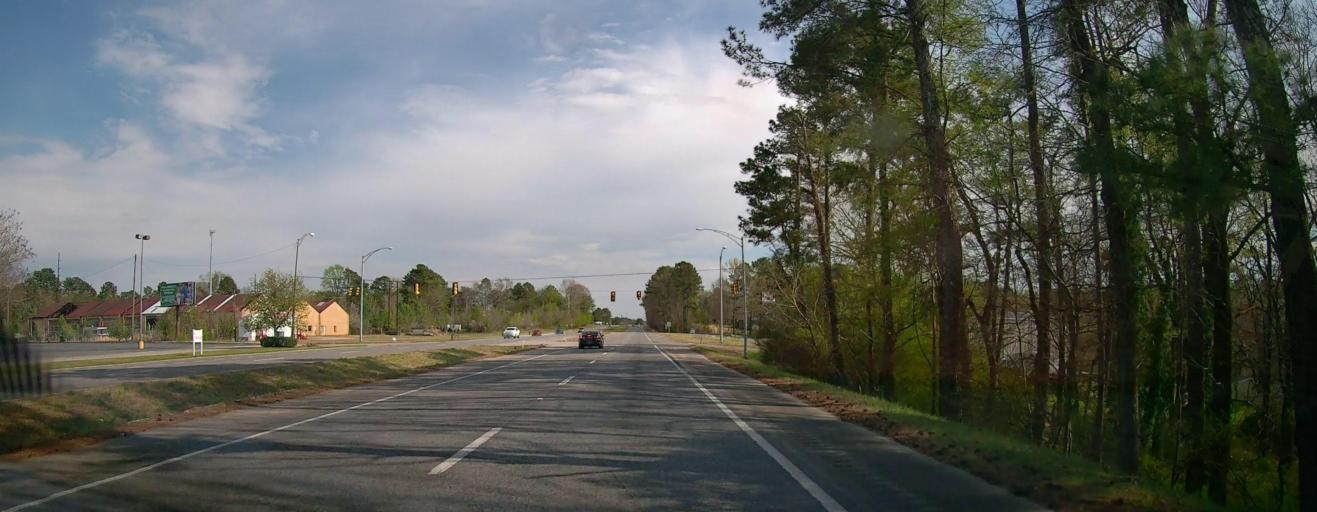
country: US
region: Alabama
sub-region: Jefferson County
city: Adamsville
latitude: 33.5951
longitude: -86.9417
